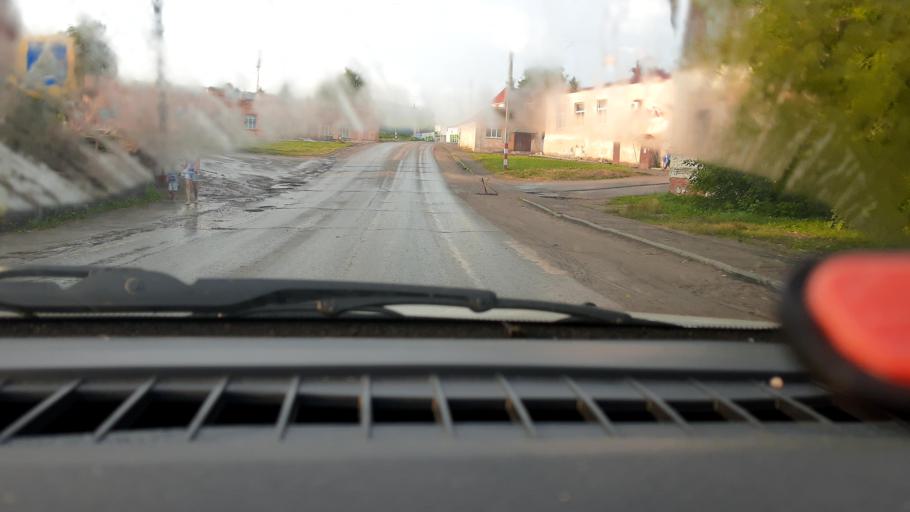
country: RU
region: Nizjnij Novgorod
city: Lukoyanov
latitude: 55.0307
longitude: 44.4931
